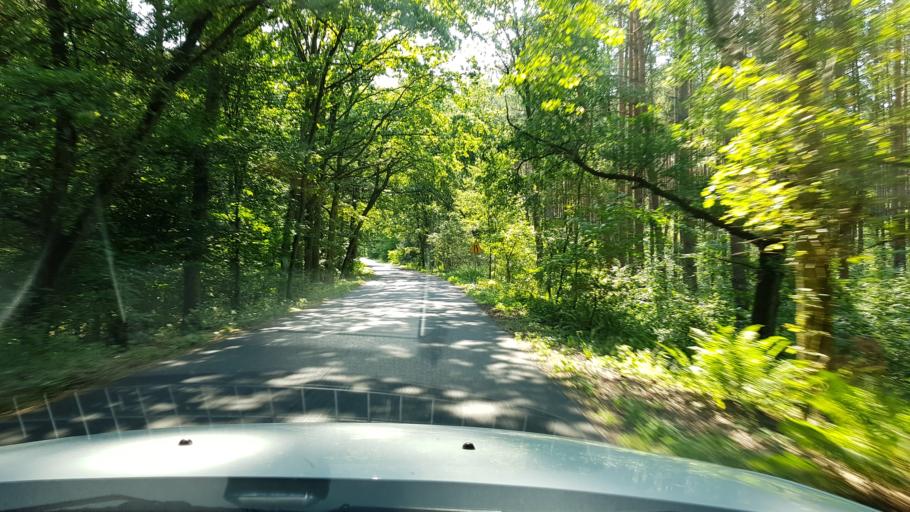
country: PL
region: West Pomeranian Voivodeship
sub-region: Powiat gryfinski
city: Chojna
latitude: 52.9383
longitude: 14.5161
